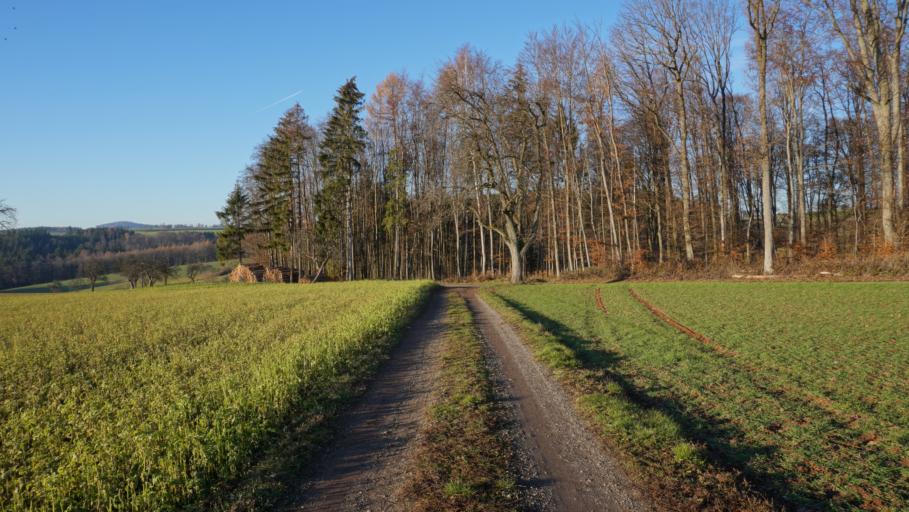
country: DE
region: Baden-Wuerttemberg
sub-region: Karlsruhe Region
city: Neckargerach
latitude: 49.4495
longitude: 9.0941
